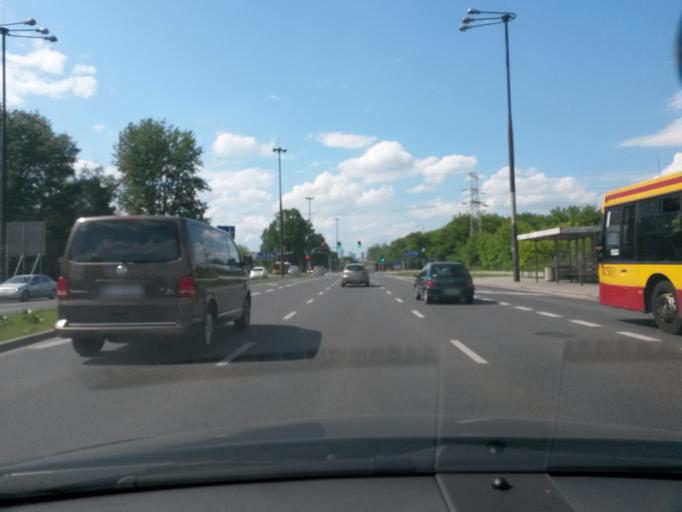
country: PL
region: Masovian Voivodeship
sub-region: Warszawa
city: Mokotow
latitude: 52.1909
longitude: 21.0462
